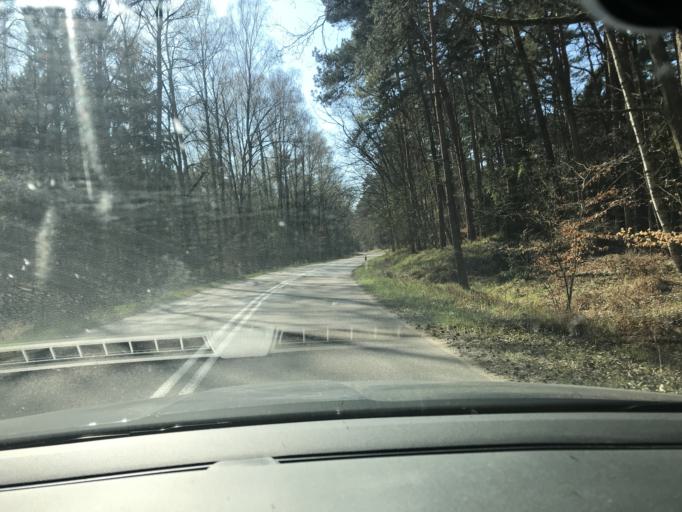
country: PL
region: Pomeranian Voivodeship
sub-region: Powiat nowodworski
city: Krynica Morska
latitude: 54.3613
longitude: 19.3565
